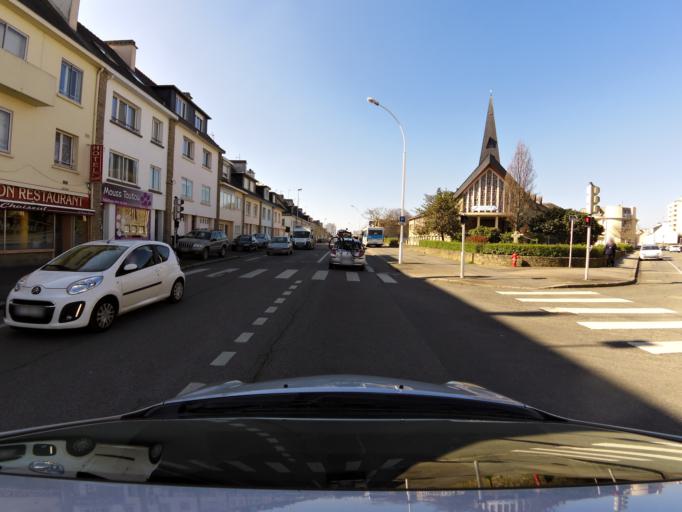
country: FR
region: Brittany
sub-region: Departement du Morbihan
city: Lorient
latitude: 47.7514
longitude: -3.3718
